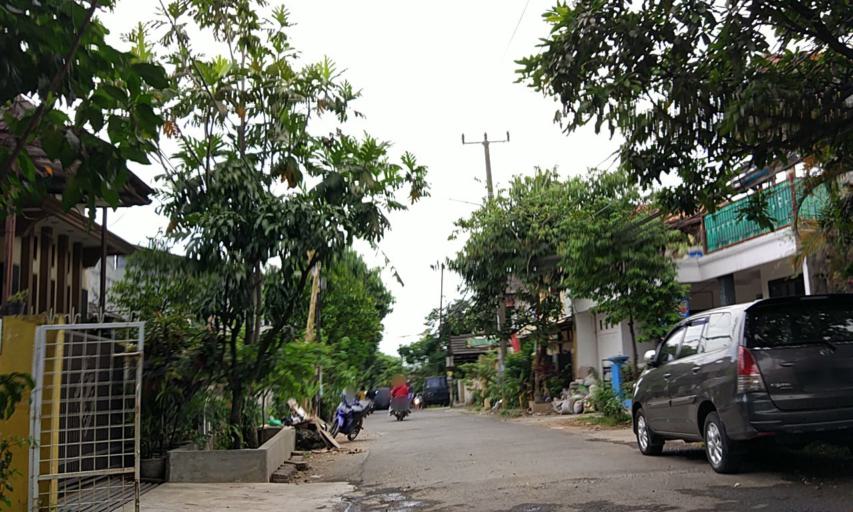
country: ID
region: West Java
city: Cileunyi
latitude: -6.9039
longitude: 107.6972
